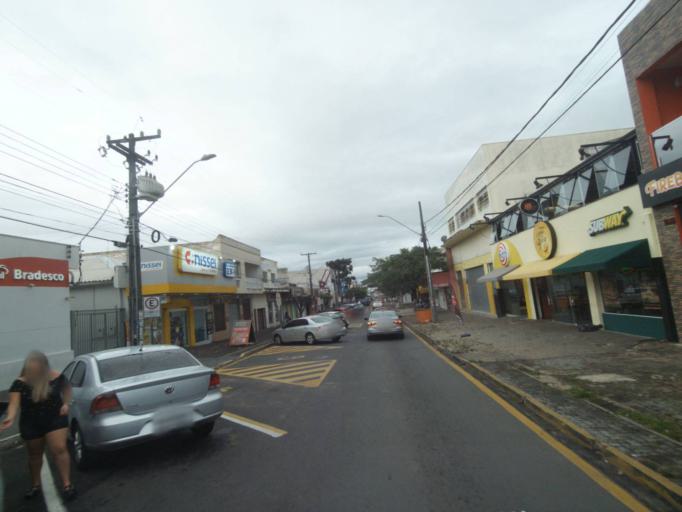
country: BR
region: Parana
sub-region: Telemaco Borba
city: Telemaco Borba
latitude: -24.3256
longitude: -50.6228
